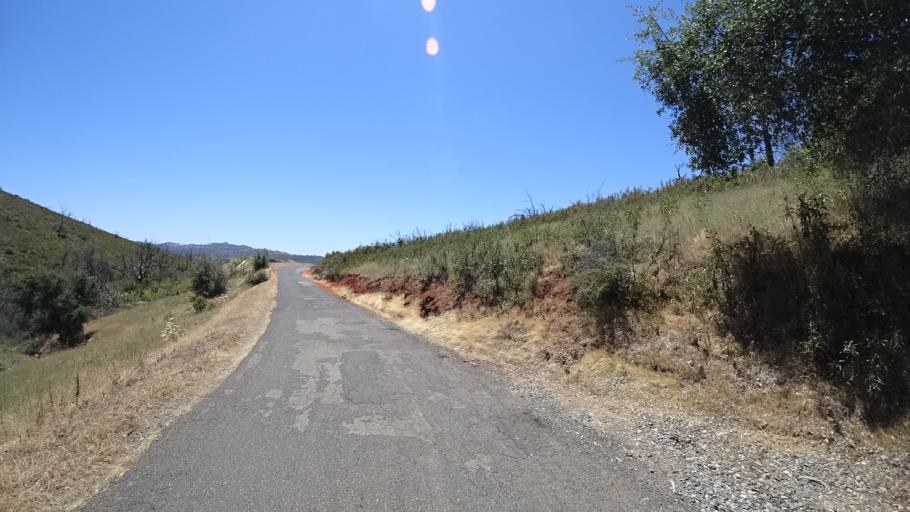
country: US
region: California
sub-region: Calaveras County
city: Mountain Ranch
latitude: 38.2896
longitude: -120.6111
